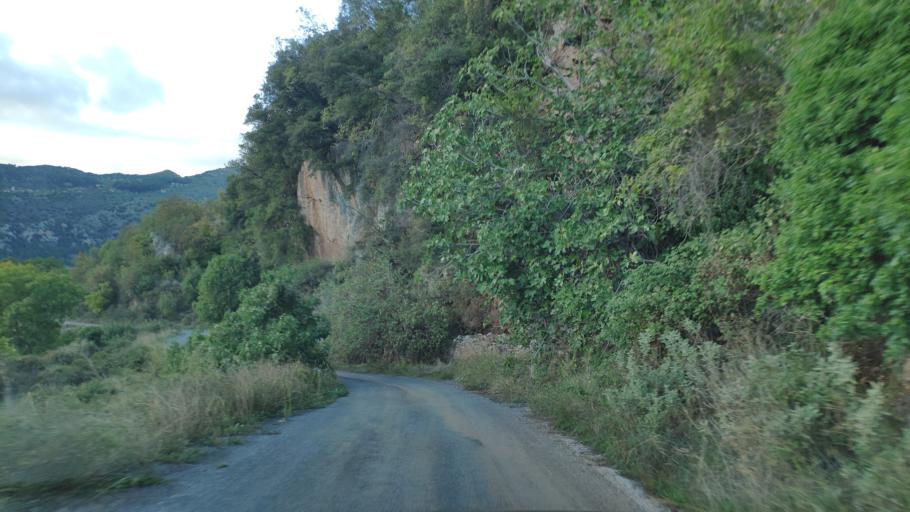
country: GR
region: Peloponnese
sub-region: Nomos Arkadias
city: Dimitsana
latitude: 37.5805
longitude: 22.0459
